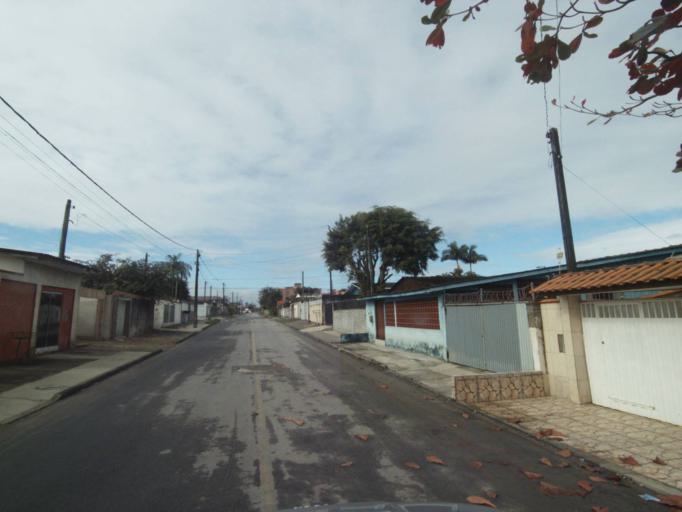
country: BR
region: Parana
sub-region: Paranagua
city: Paranagua
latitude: -25.5663
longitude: -48.5738
